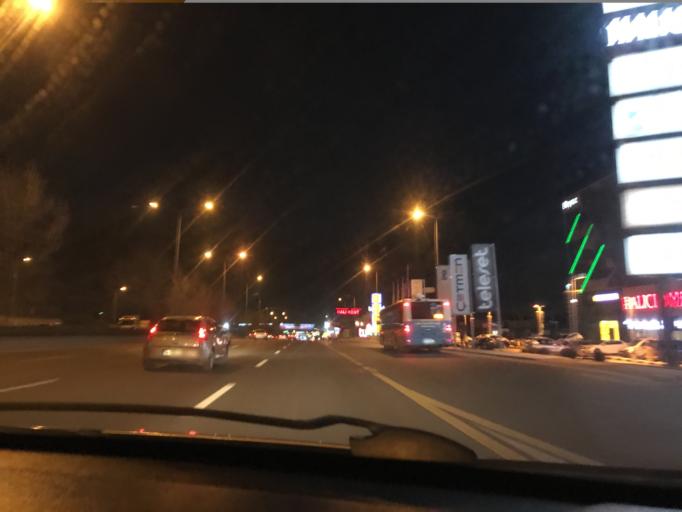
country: TR
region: Ankara
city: Batikent
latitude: 39.9454
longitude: 32.7290
